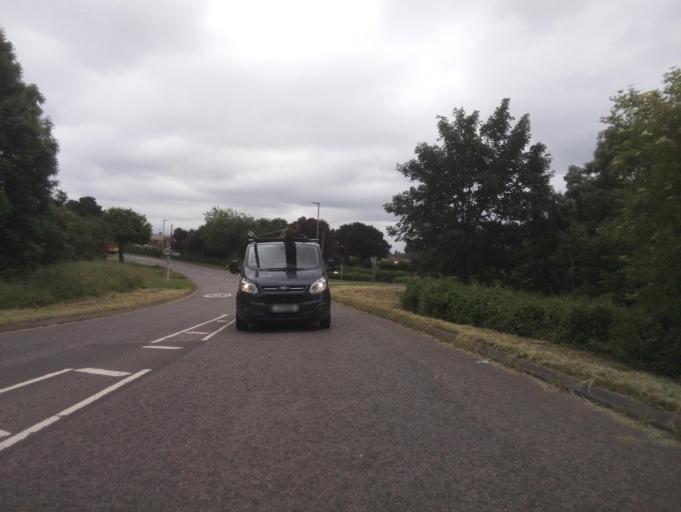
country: GB
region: England
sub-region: Leicestershire
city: Asfordby
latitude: 52.7664
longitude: -0.9631
